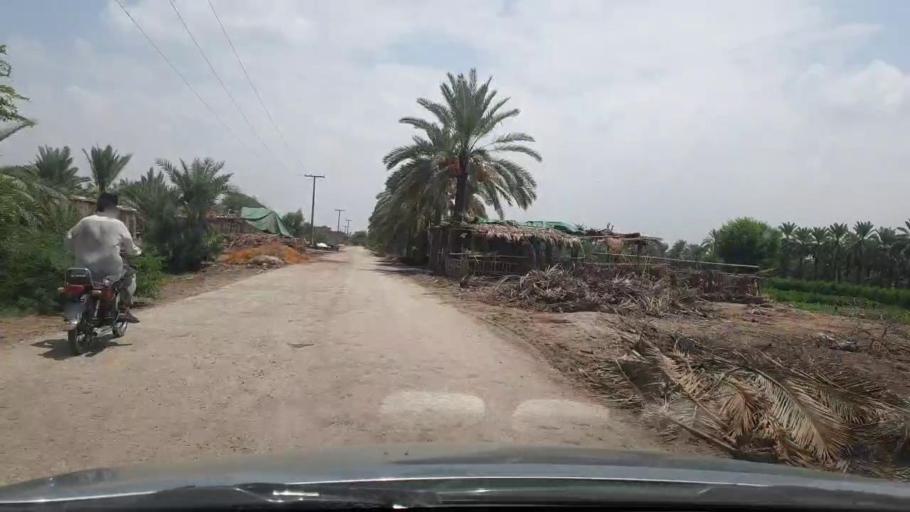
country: PK
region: Sindh
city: Khairpur
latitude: 27.4368
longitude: 68.7573
